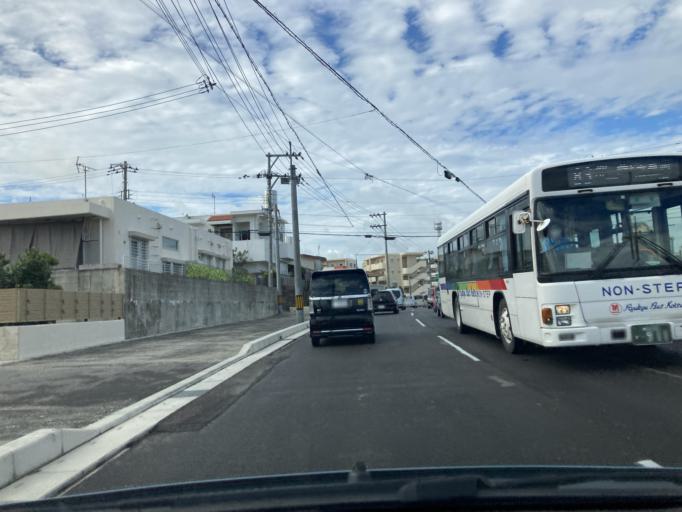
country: JP
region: Okinawa
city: Tomigusuku
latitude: 26.1519
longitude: 127.7218
